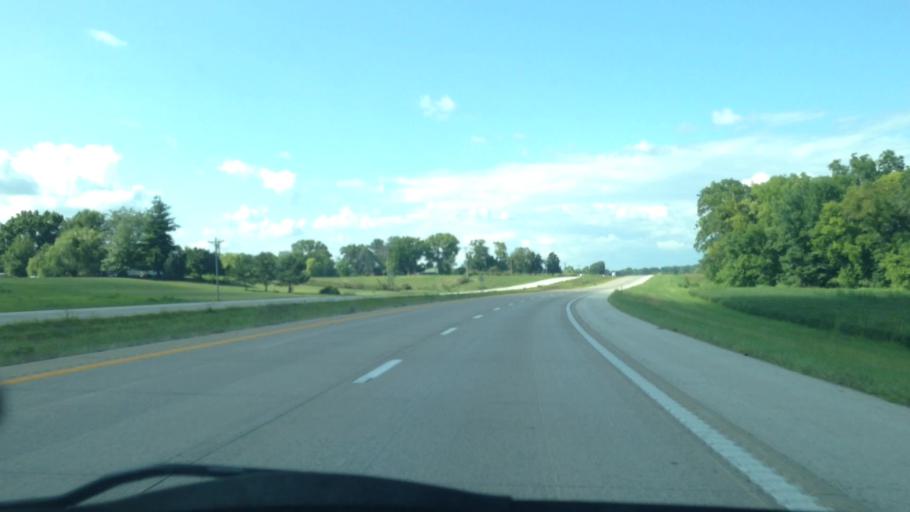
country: US
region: Missouri
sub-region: Lewis County
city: Canton
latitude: 40.2464
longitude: -91.5391
